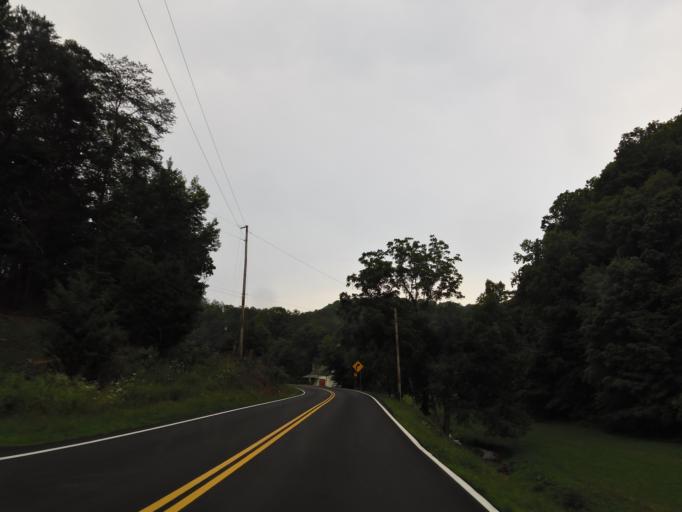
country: US
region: Tennessee
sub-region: Sevier County
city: Sevierville
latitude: 35.8267
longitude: -83.6266
